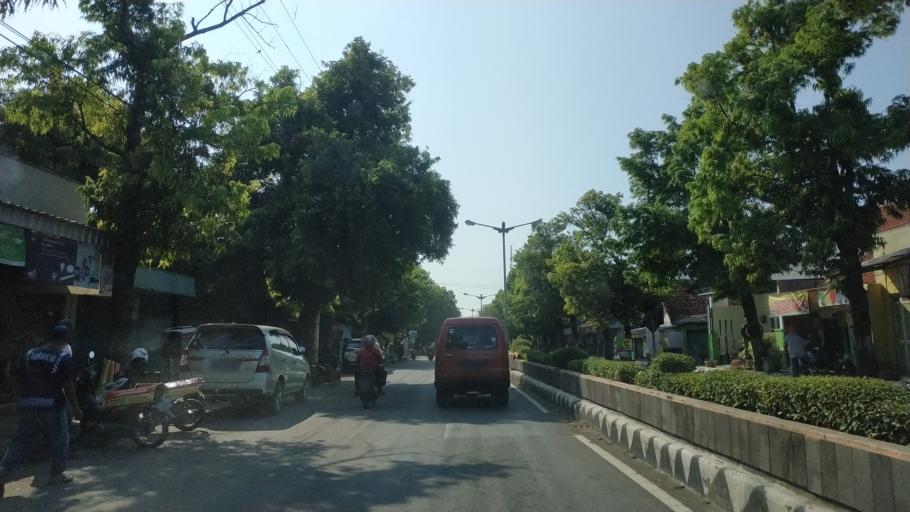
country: ID
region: Central Java
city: Petarukan
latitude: -6.8939
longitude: 109.4141
